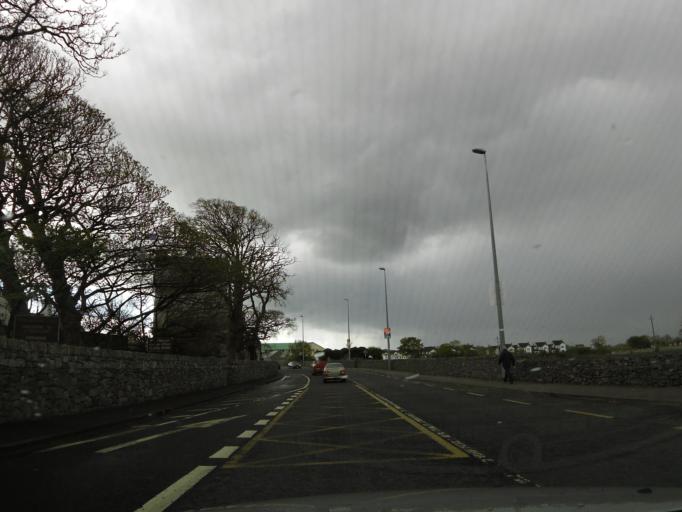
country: IE
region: Connaught
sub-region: County Galway
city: Claregalway
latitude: 53.3470
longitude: -8.9416
